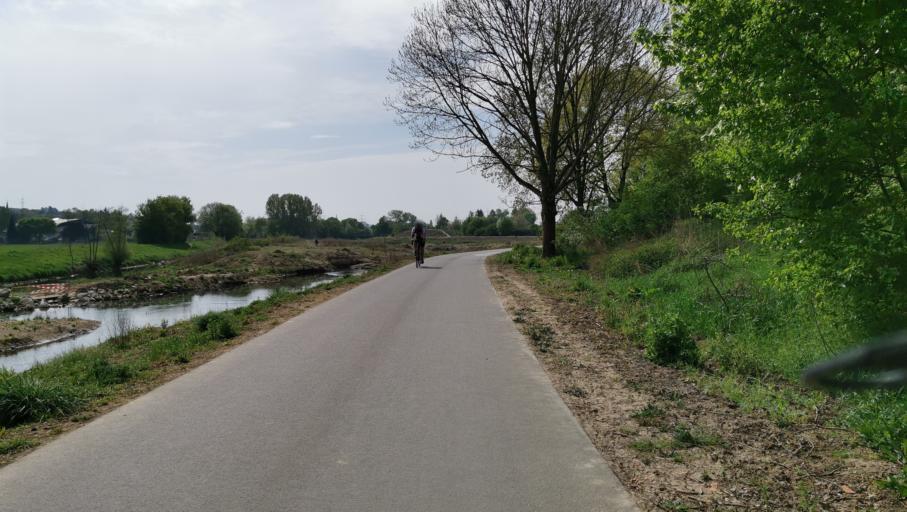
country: DE
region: Hesse
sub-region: Regierungsbezirk Darmstadt
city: Karben
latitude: 50.2276
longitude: 8.7656
